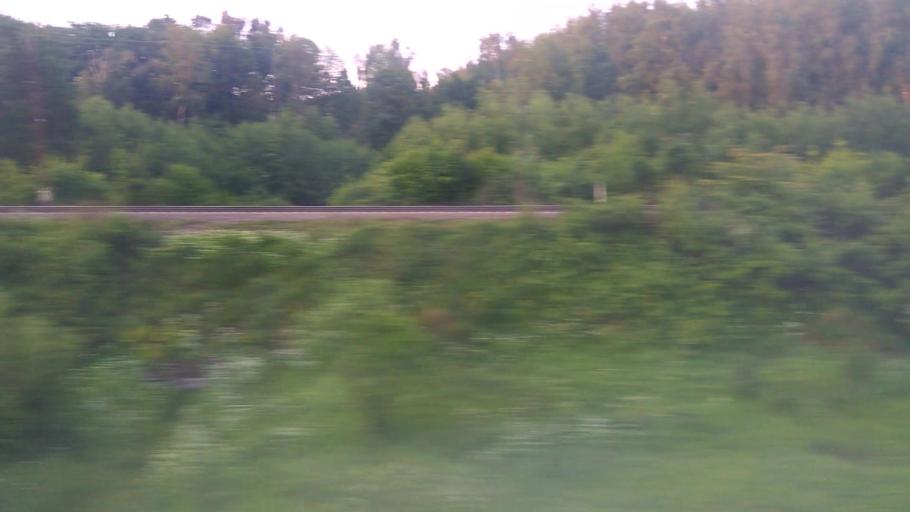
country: RU
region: Moskovskaya
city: Belyye Stolby
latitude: 55.3043
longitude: 37.8764
